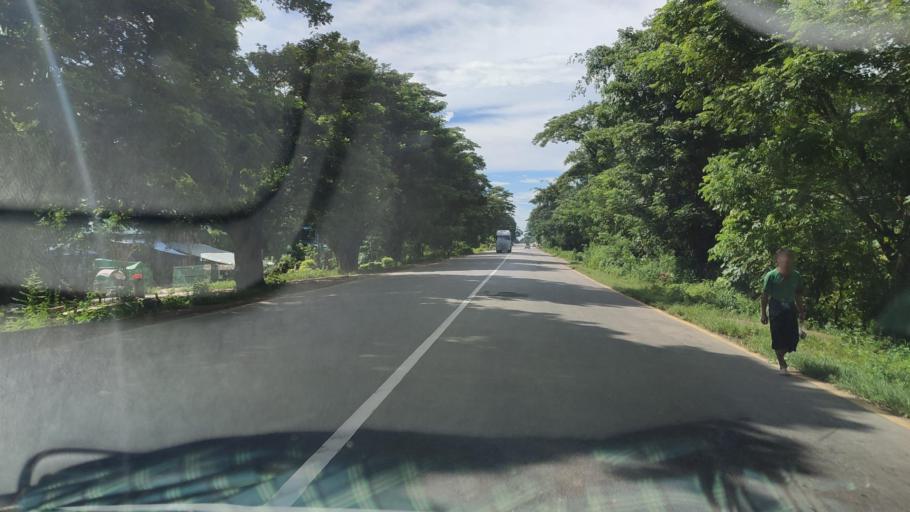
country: MM
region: Bago
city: Pyu
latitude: 18.3057
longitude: 96.5077
